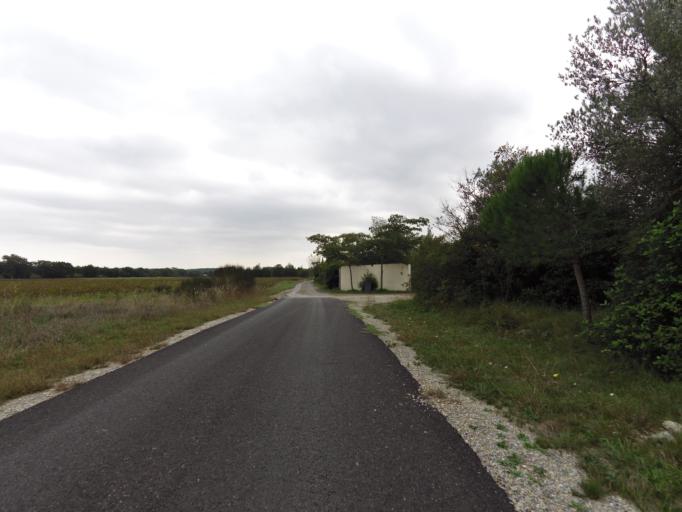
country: FR
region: Languedoc-Roussillon
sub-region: Departement de l'Herault
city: Villetelle
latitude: 43.7384
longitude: 4.1316
